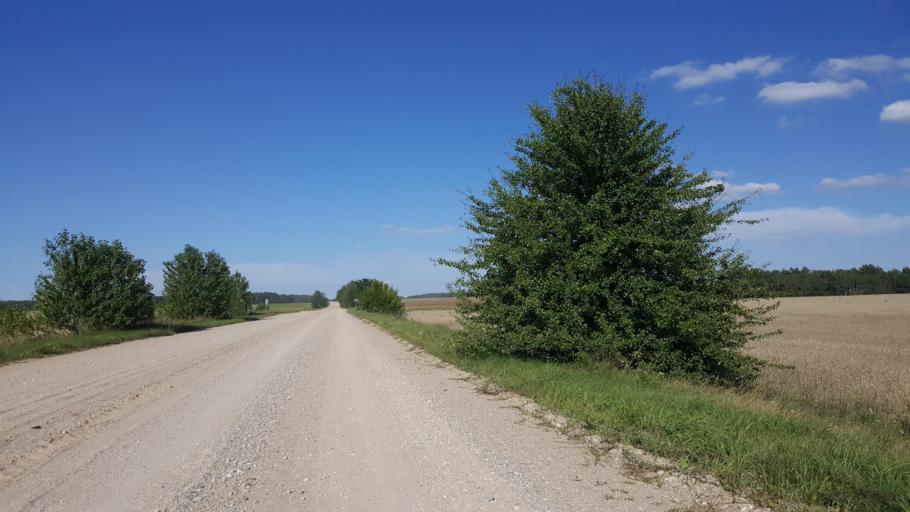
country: BY
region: Brest
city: Kamyanyets
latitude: 52.3572
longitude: 23.6979
